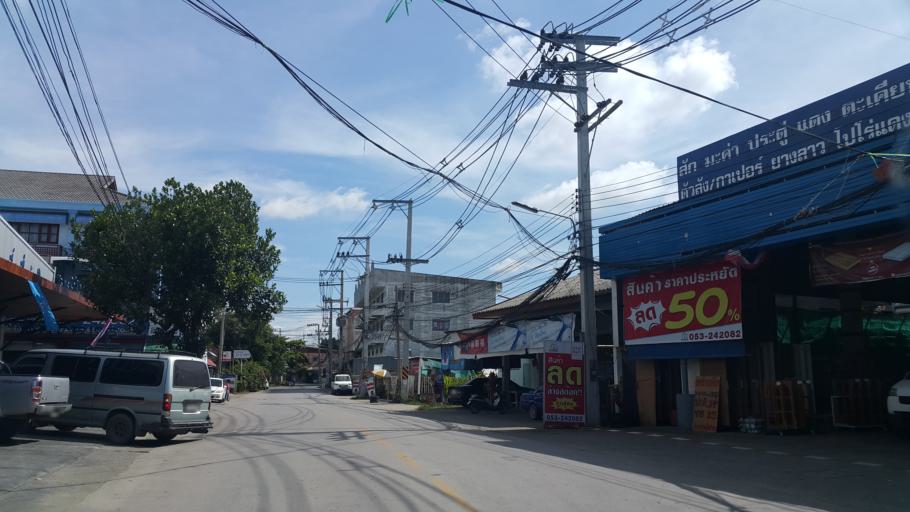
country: TH
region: Chiang Mai
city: Chiang Mai
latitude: 18.8056
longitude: 99.0124
